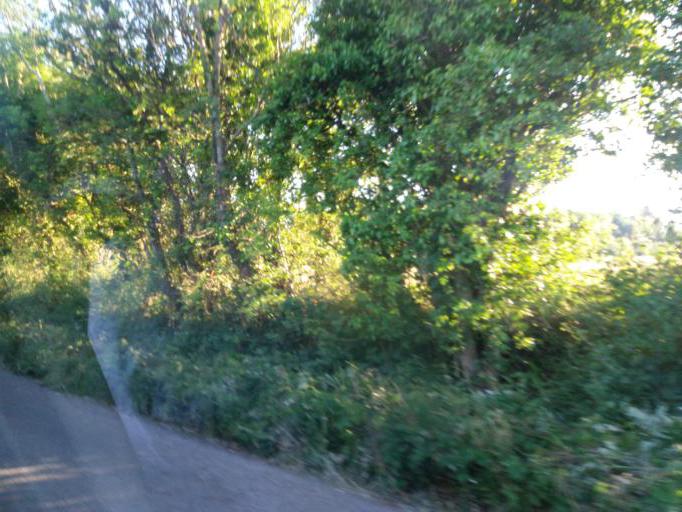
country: IE
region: Leinster
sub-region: An Mhi
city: Ashbourne
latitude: 53.5698
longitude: -6.3511
